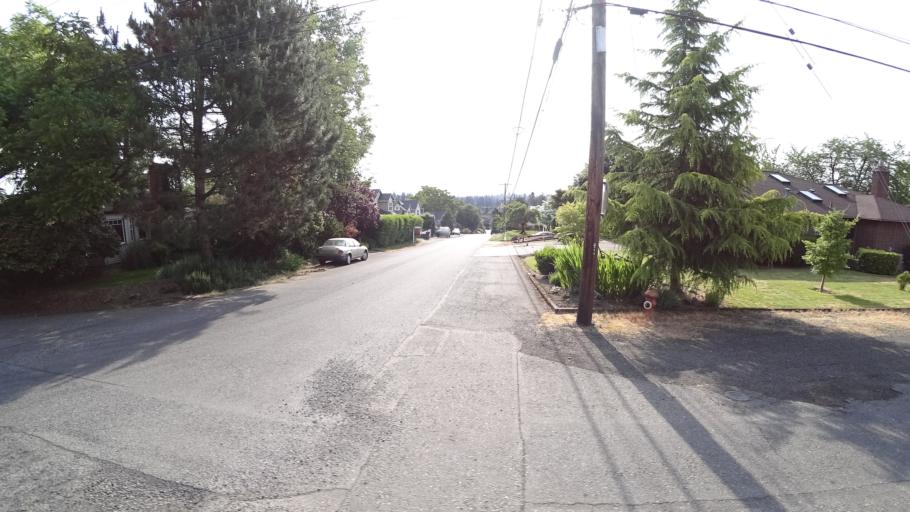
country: US
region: Oregon
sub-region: Washington County
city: Garden Home-Whitford
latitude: 45.4584
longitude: -122.7135
